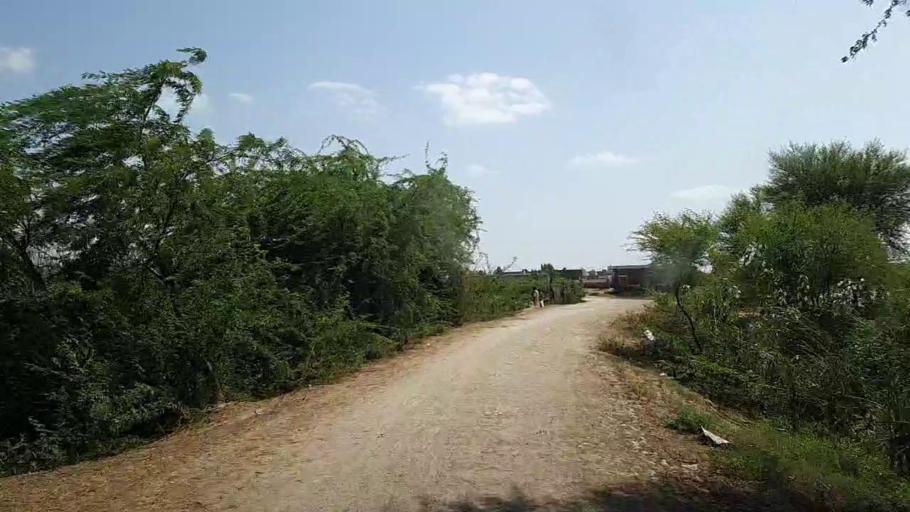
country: PK
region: Sindh
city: Kario
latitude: 24.6419
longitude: 68.5682
